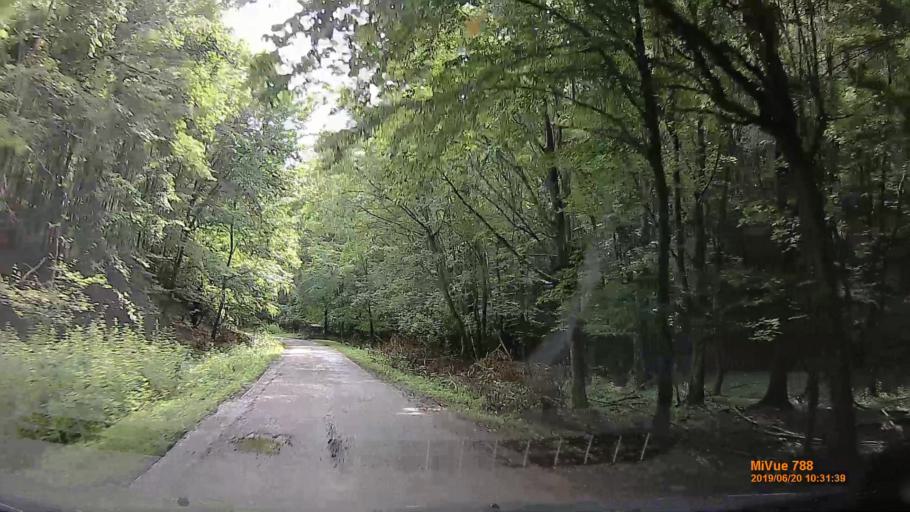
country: HU
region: Baranya
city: Mecseknadasd
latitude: 46.2074
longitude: 18.5105
